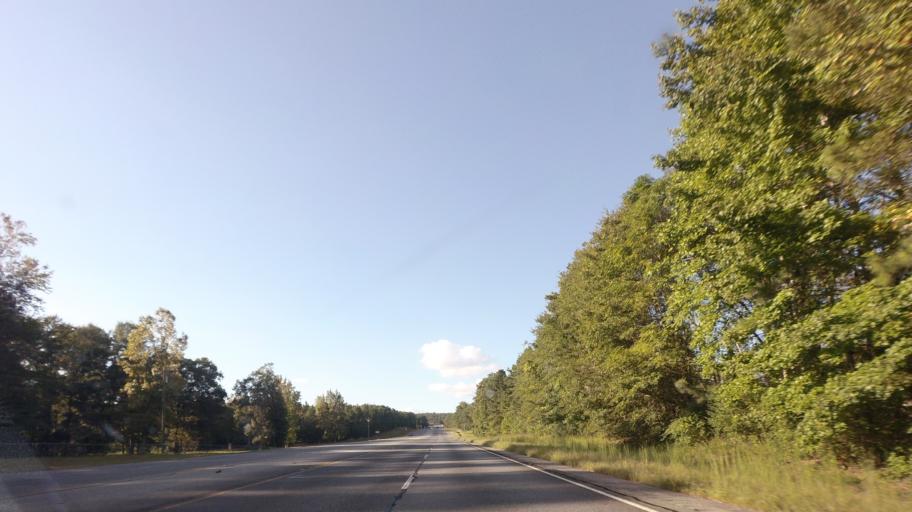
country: US
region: Georgia
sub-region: Upson County
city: Hannahs Mill
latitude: 32.9862
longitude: -84.3178
